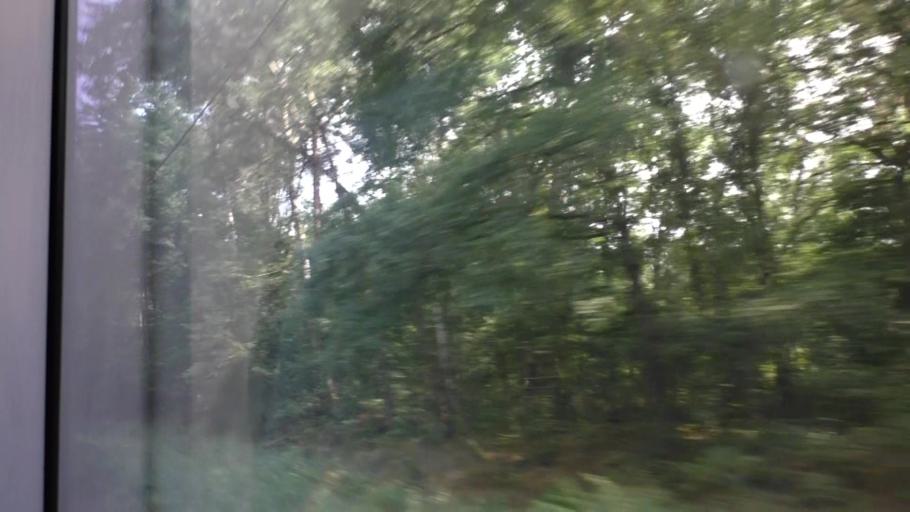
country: DE
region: Brandenburg
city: Bestensee
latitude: 52.2969
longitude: 13.7476
